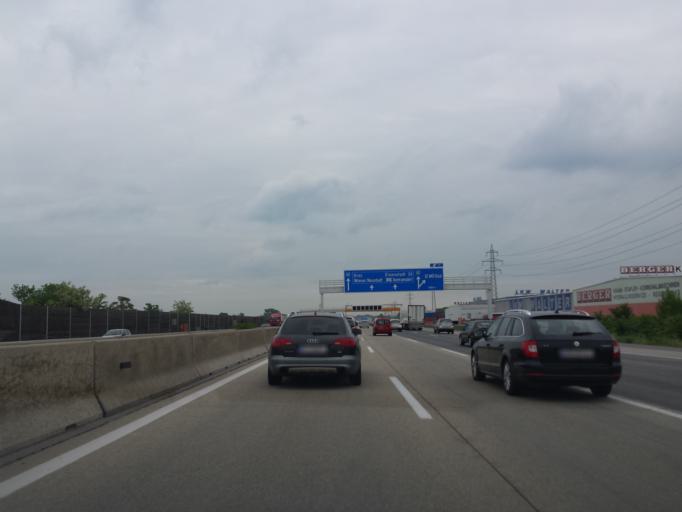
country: AT
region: Lower Austria
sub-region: Politischer Bezirk Modling
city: Biedermannsdorf
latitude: 48.0726
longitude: 16.3380
